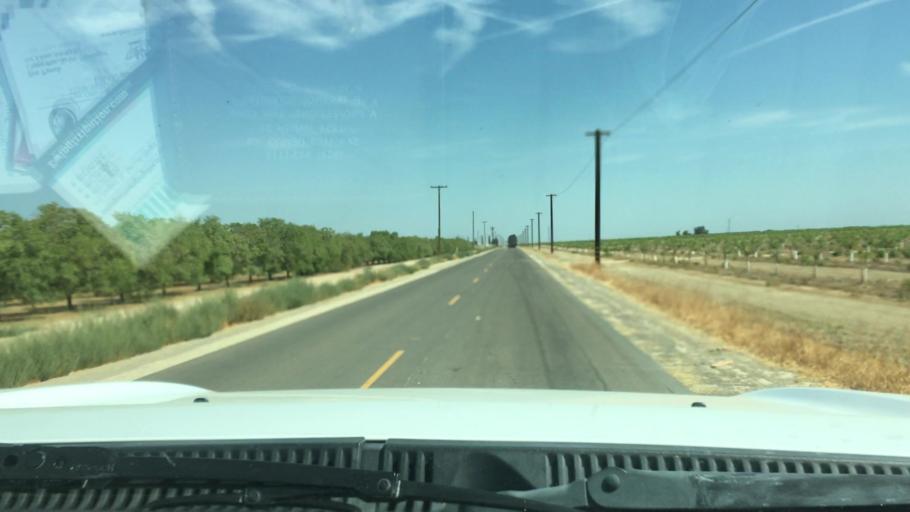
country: US
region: California
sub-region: Kern County
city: Shafter
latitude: 35.4521
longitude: -119.3681
